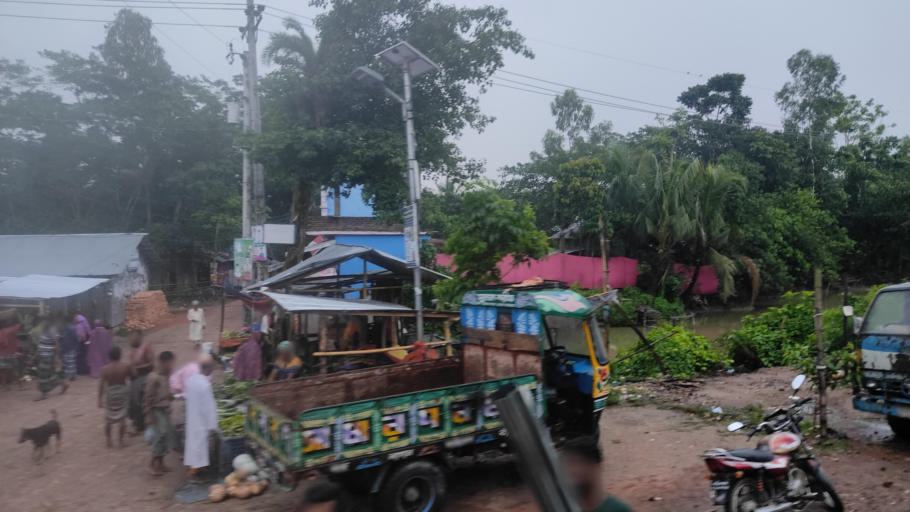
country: BD
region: Barisal
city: Bhandaria
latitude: 22.2935
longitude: 90.3253
